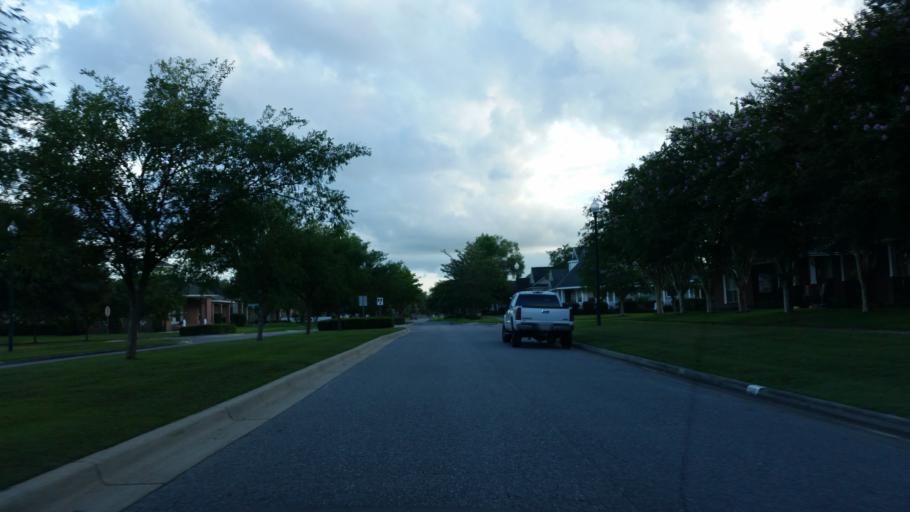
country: US
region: Florida
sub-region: Escambia County
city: Ensley
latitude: 30.5359
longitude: -87.3078
